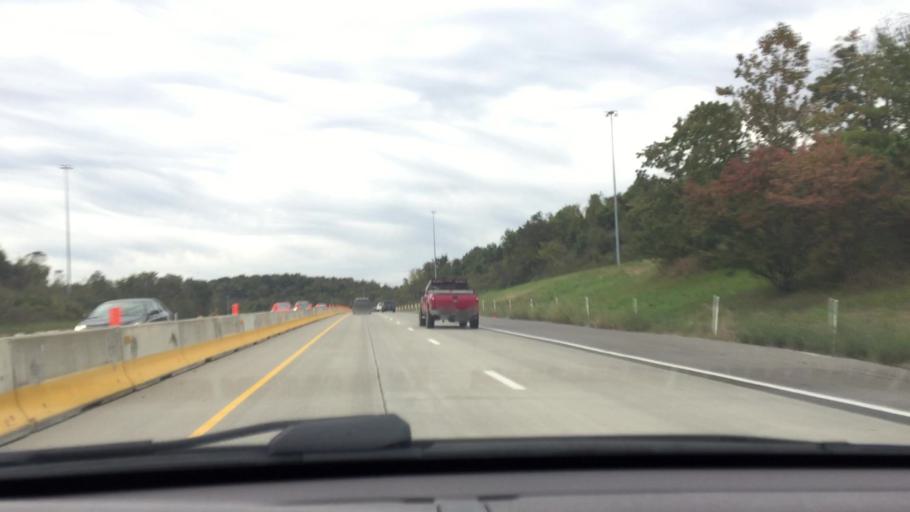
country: US
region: Pennsylvania
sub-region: Allegheny County
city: Enlow
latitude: 40.4721
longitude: -80.2232
